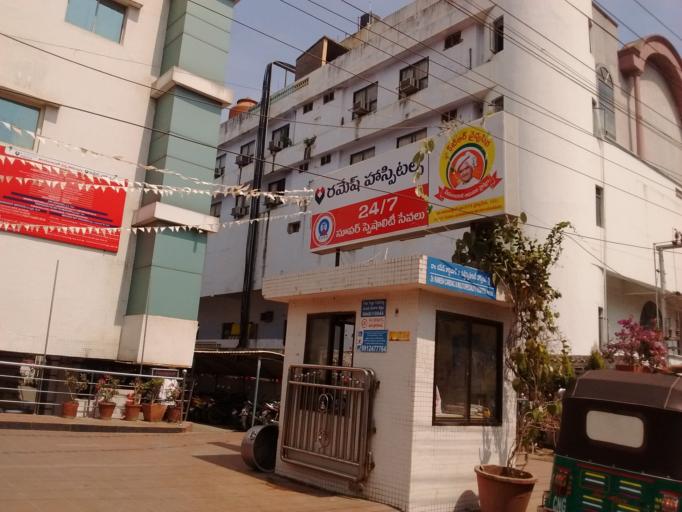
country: IN
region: Andhra Pradesh
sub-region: Krishna
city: Yanamalakuduru
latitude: 16.5055
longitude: 80.6602
